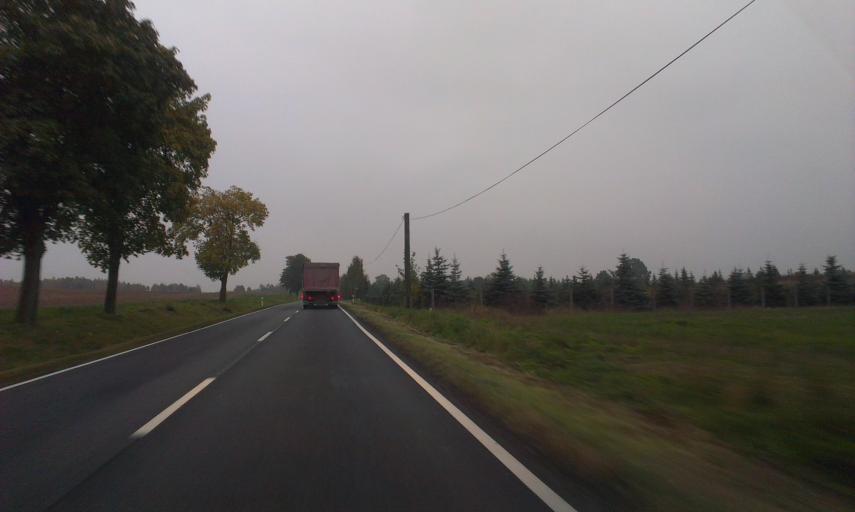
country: PL
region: Kujawsko-Pomorskie
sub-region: Powiat sepolenski
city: Sosno
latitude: 53.4383
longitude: 17.6171
